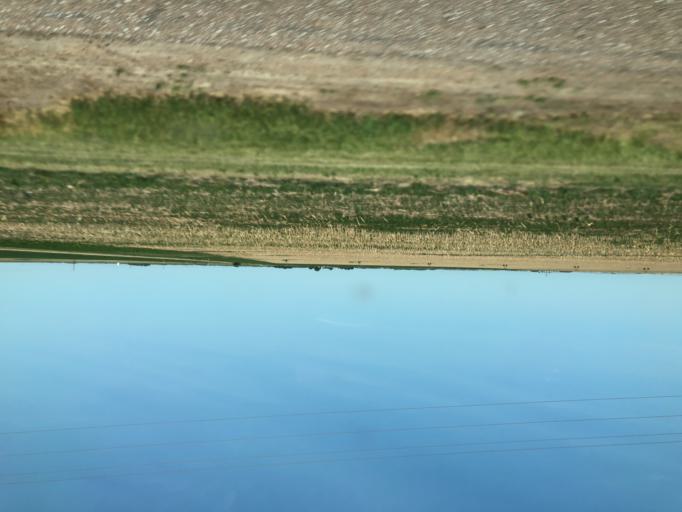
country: US
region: Nebraska
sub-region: Fillmore County
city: Geneva
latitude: 40.4523
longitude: -97.5960
